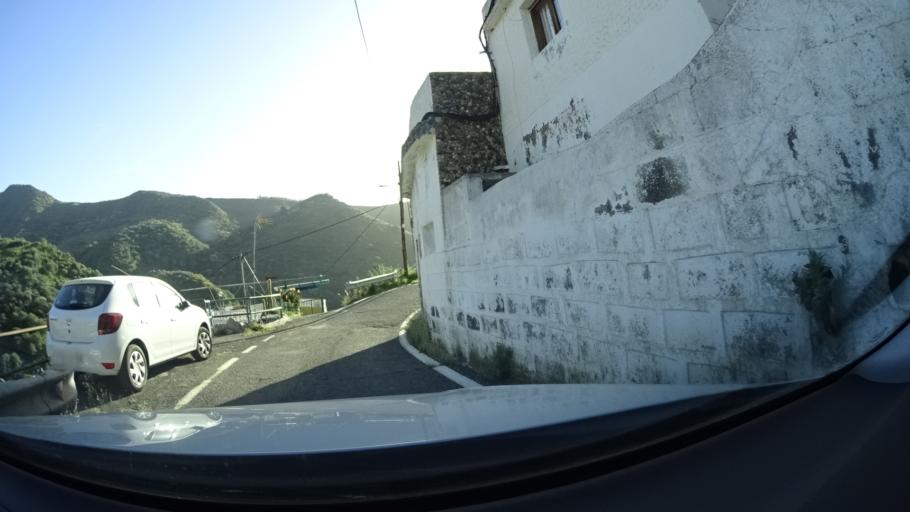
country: ES
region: Canary Islands
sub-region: Provincia de Las Palmas
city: Artenara
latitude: 28.0431
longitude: -15.6511
